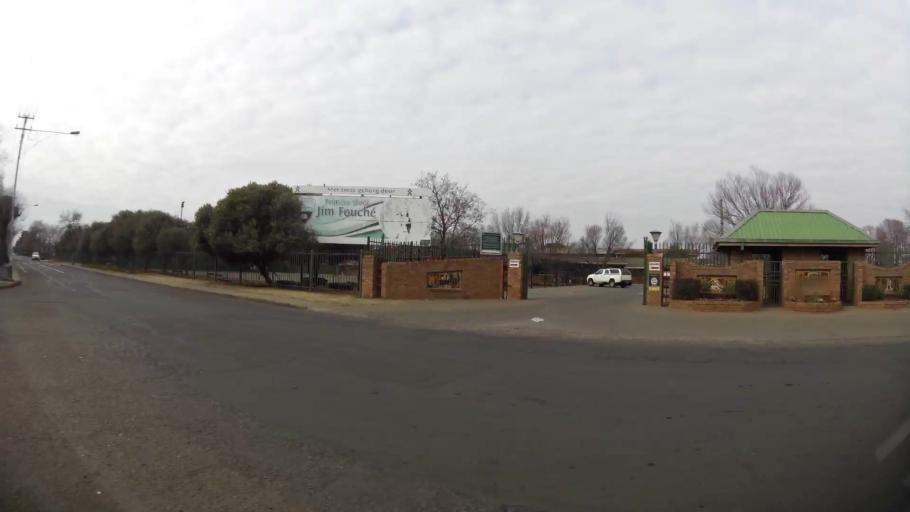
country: ZA
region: Orange Free State
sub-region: Mangaung Metropolitan Municipality
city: Bloemfontein
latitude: -29.1277
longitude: 26.1724
